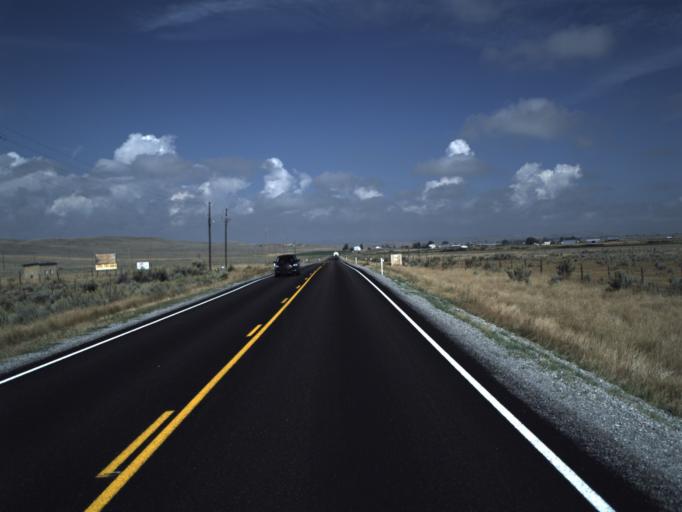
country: US
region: Utah
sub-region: Rich County
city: Randolph
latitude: 41.5860
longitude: -111.1686
